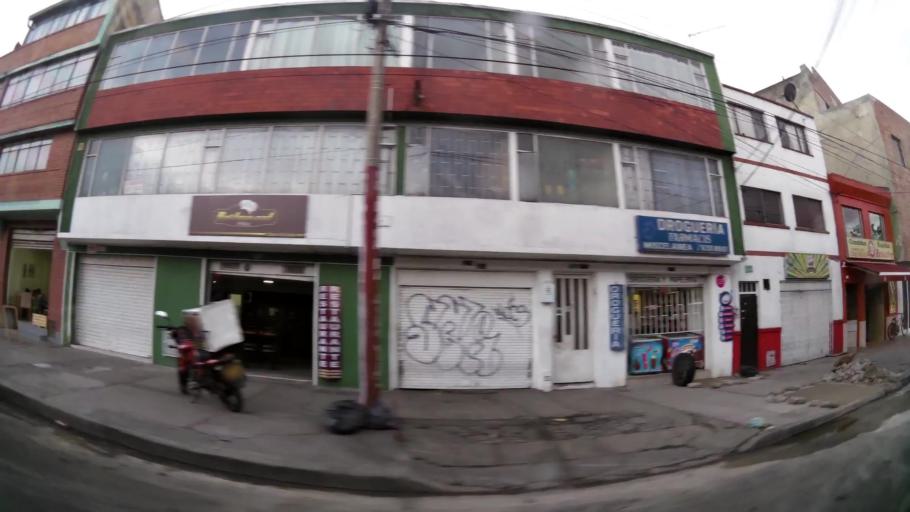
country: CO
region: Bogota D.C.
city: Barrio San Luis
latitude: 4.6773
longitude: -74.0738
